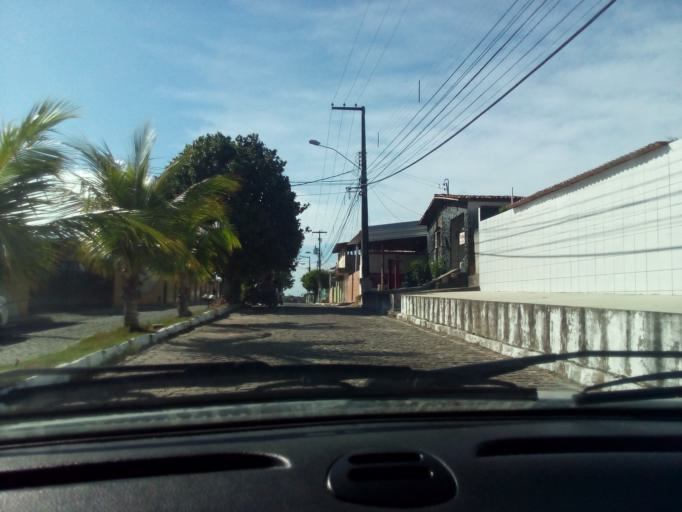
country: BR
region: Rio Grande do Norte
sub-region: Parnamirim
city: Parnamirim
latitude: -5.8865
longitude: -35.2024
